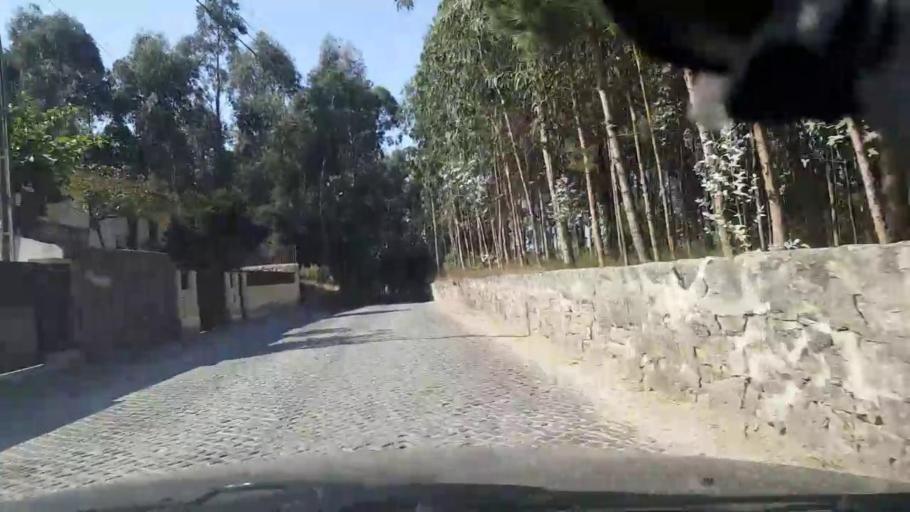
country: PT
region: Porto
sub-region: Vila do Conde
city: Arvore
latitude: 41.3836
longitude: -8.6846
